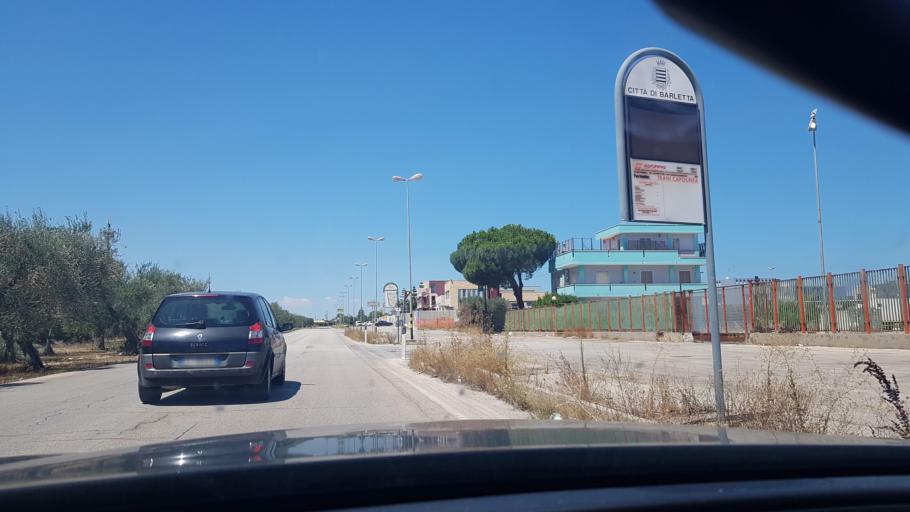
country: IT
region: Apulia
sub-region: Provincia di Barletta - Andria - Trani
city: Barletta
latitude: 41.3019
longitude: 16.3266
